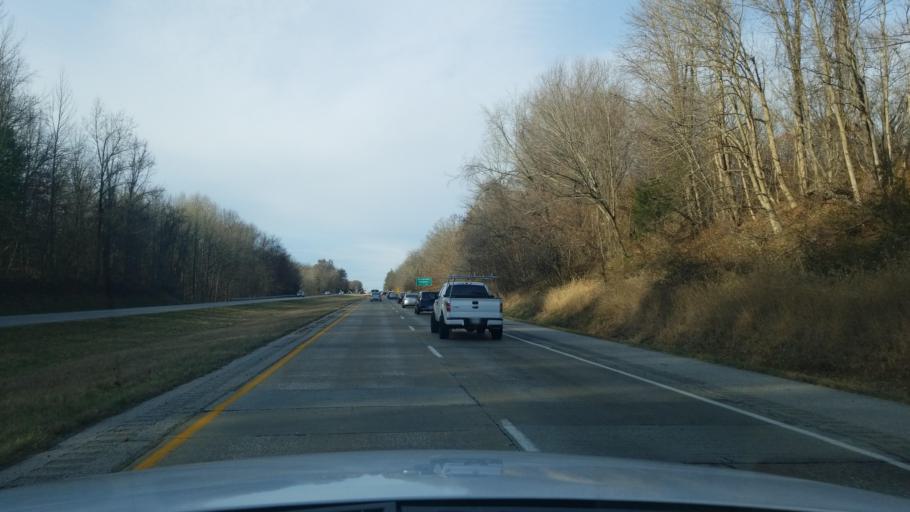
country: US
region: Indiana
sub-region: Vanderburgh County
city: Evansville
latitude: 37.9731
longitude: -87.6520
